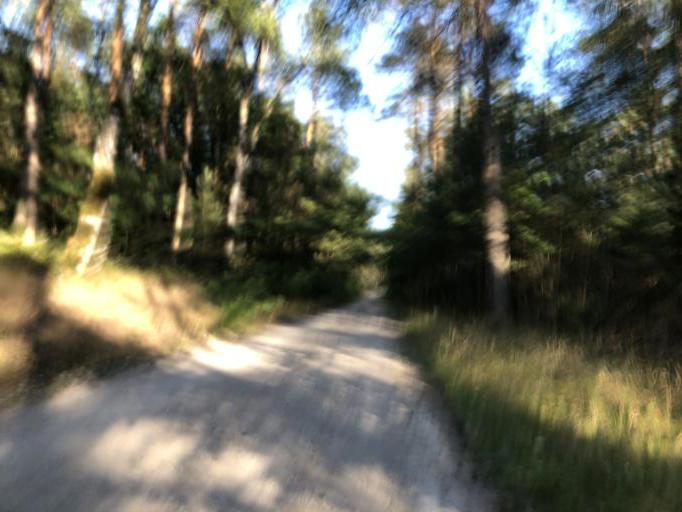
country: DE
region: Bavaria
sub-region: Regierungsbezirk Mittelfranken
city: Kalchreuth
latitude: 49.5441
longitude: 11.0887
